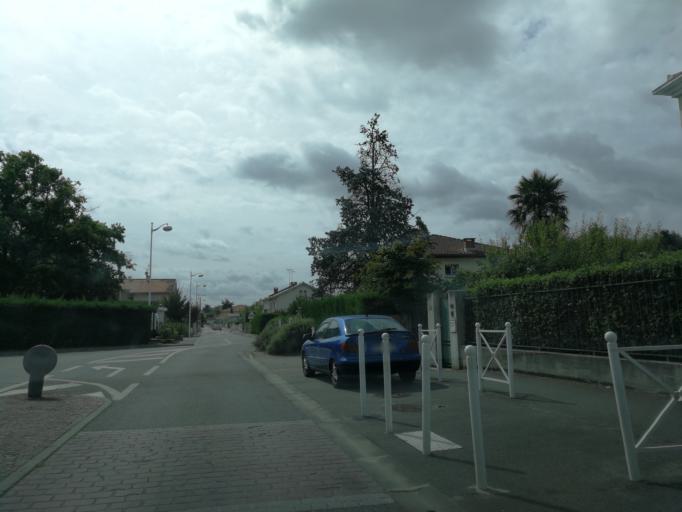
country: FR
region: Midi-Pyrenees
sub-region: Departement de la Haute-Garonne
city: Balma
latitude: 43.6140
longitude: 1.4939
